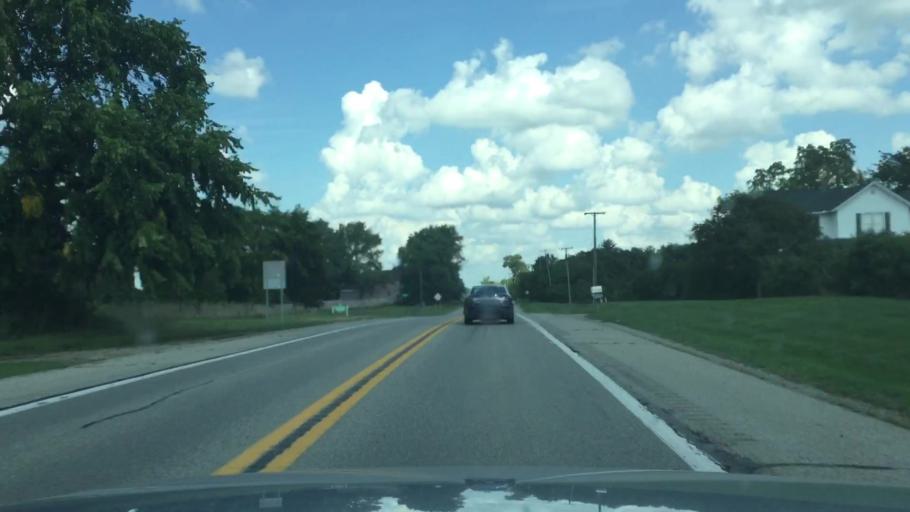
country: US
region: Michigan
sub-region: Lenawee County
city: Clinton
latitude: 42.1070
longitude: -83.8938
